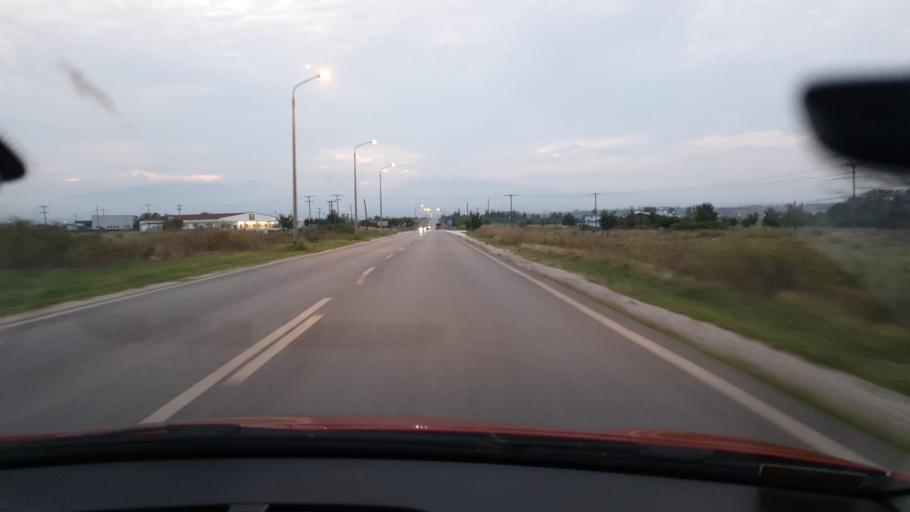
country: GR
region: Central Macedonia
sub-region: Nomos Kilkis
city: Polykastro
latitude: 40.9901
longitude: 22.6129
